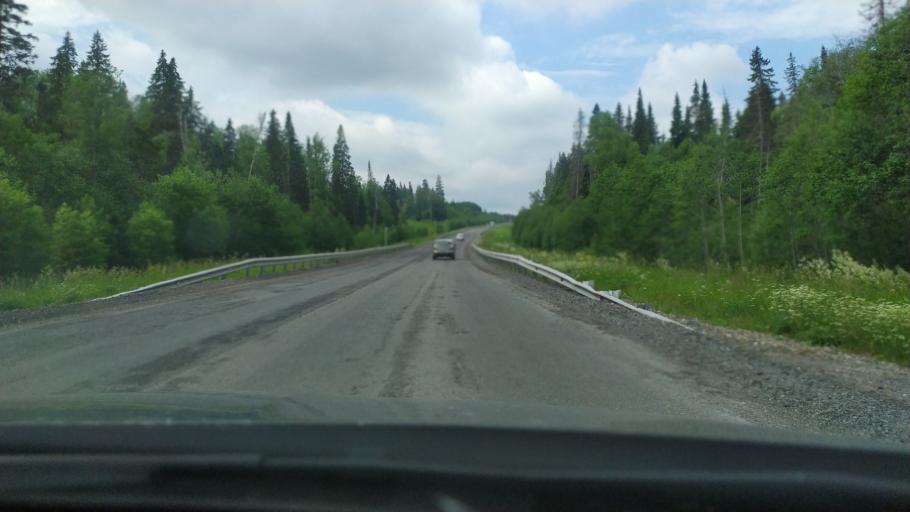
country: RU
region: Perm
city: Kalino
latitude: 58.2759
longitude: 57.3925
